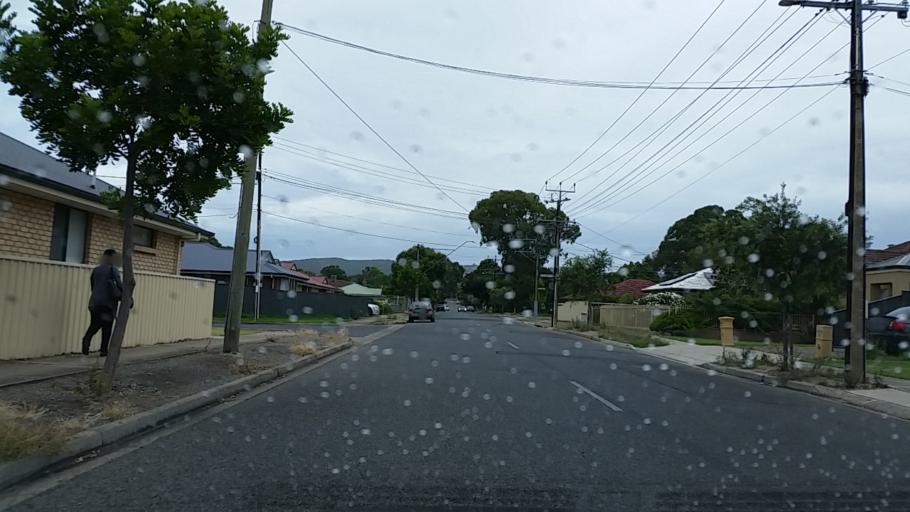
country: AU
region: South Australia
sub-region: Tea Tree Gully
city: Modbury
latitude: -34.8386
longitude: 138.6907
